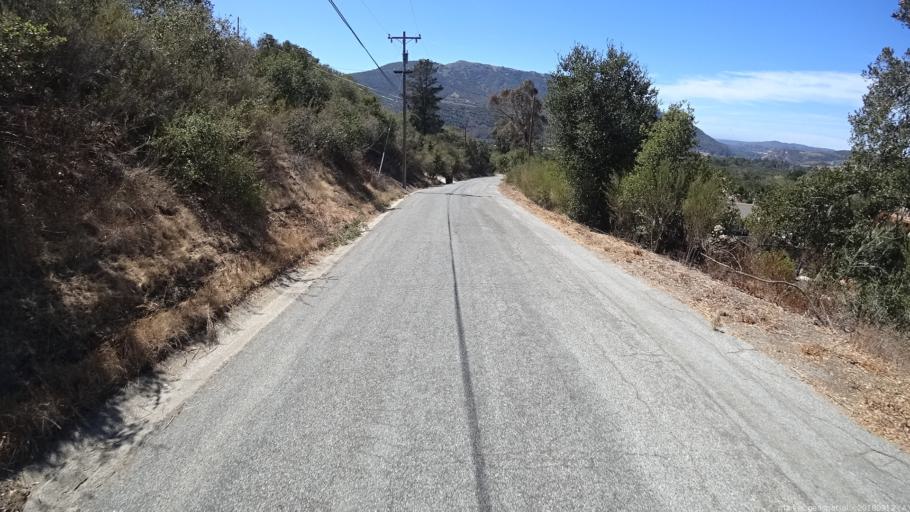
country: US
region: California
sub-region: Monterey County
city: Carmel Valley Village
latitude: 36.5011
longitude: -121.7426
